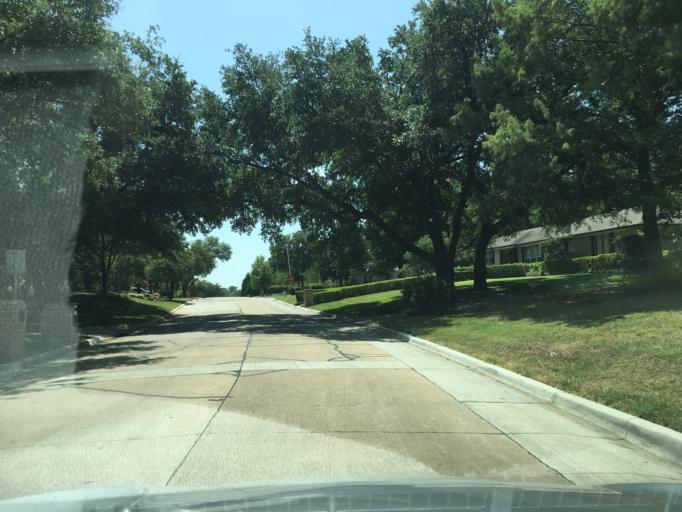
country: US
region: Texas
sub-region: Dallas County
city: Rowlett
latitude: 32.8746
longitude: -96.6054
